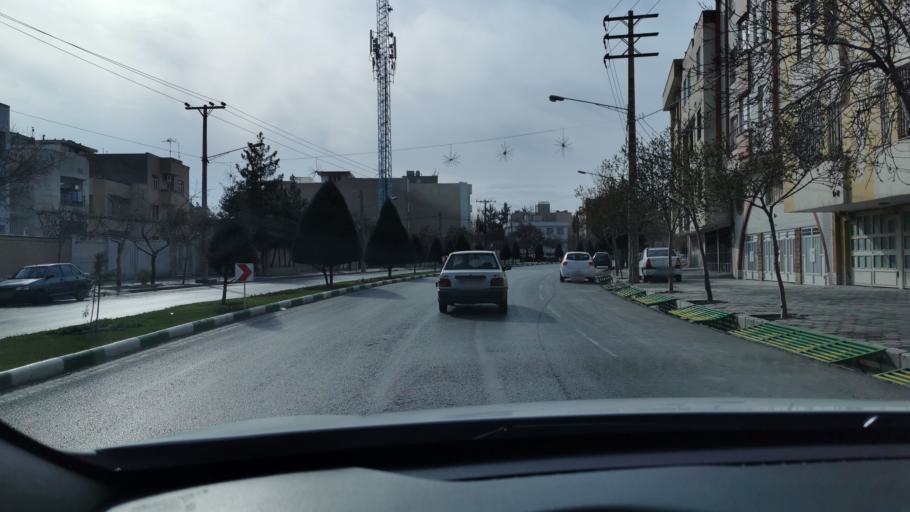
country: IR
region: Razavi Khorasan
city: Mashhad
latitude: 36.3123
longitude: 59.5155
